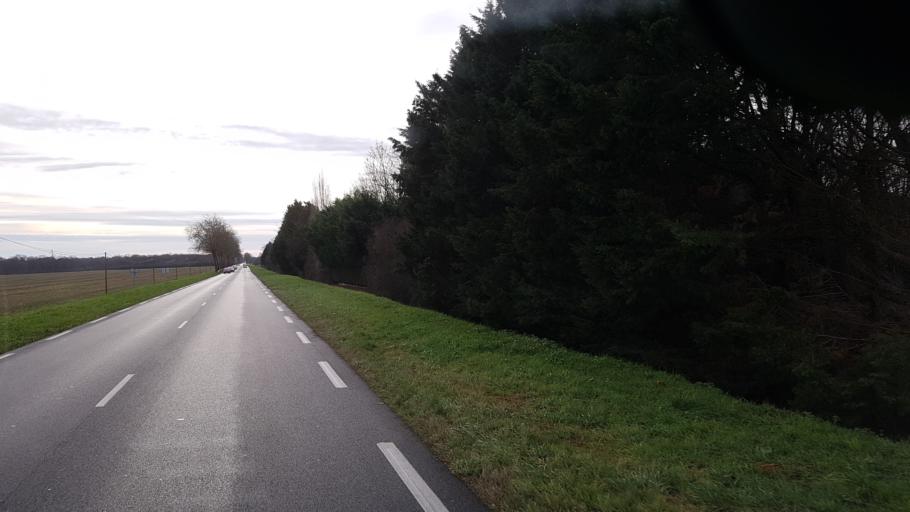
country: FR
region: Centre
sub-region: Departement du Loiret
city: Saint-Cyr-en-Val
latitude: 47.8061
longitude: 1.9299
